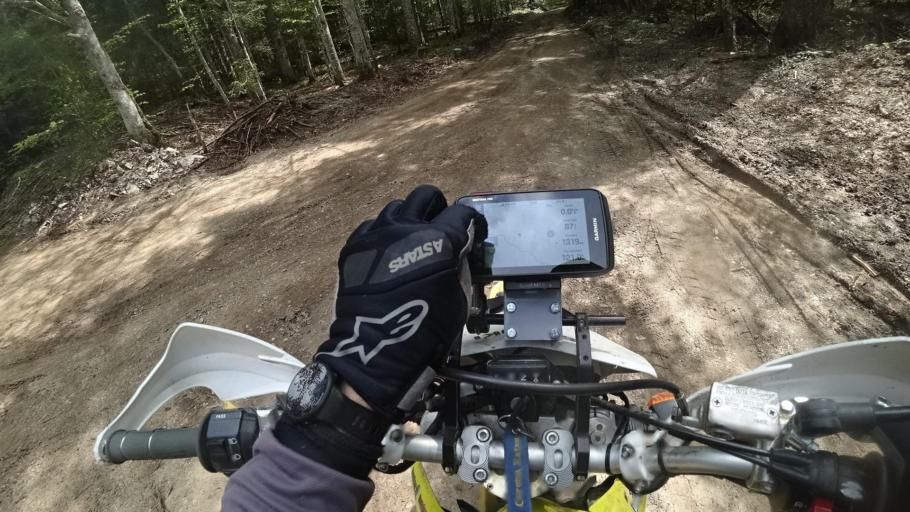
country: BA
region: Republika Srpska
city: Sipovo
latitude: 44.1585
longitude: 17.0115
